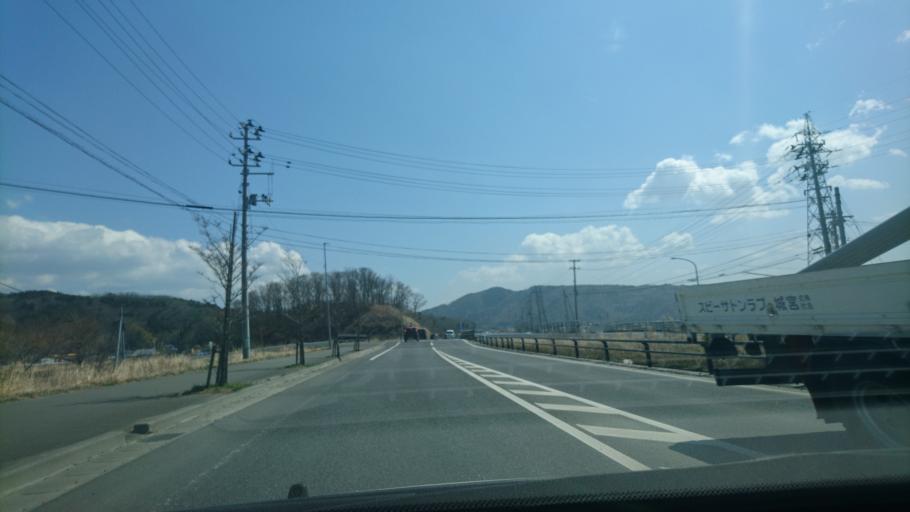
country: JP
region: Miyagi
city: Ishinomaki
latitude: 38.4544
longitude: 141.3084
